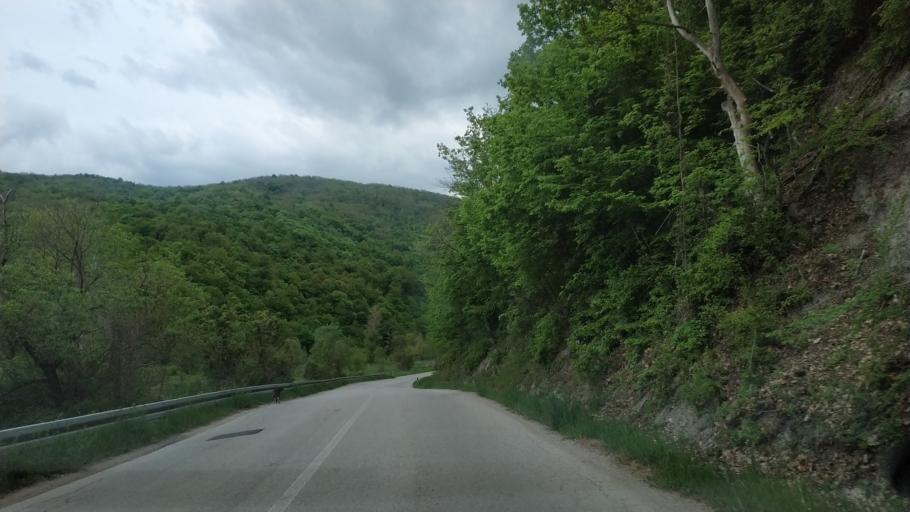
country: RS
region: Central Serbia
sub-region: Nisavski Okrug
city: Aleksinac
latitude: 43.6305
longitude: 21.7153
